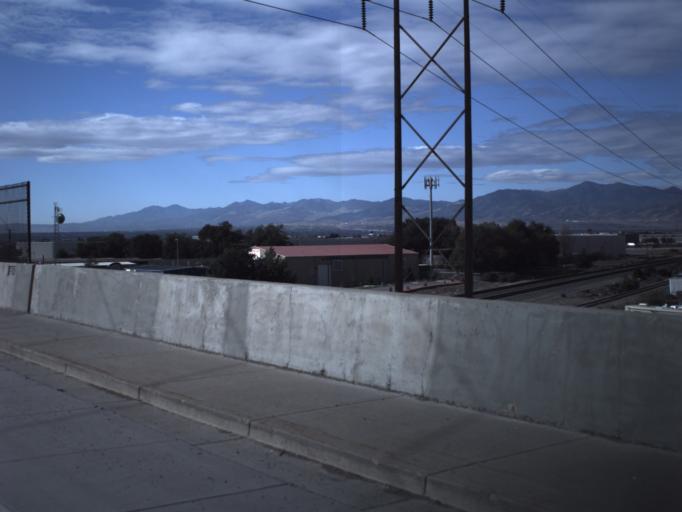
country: US
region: Utah
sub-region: Salt Lake County
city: Salt Lake City
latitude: 40.7646
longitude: -111.9392
